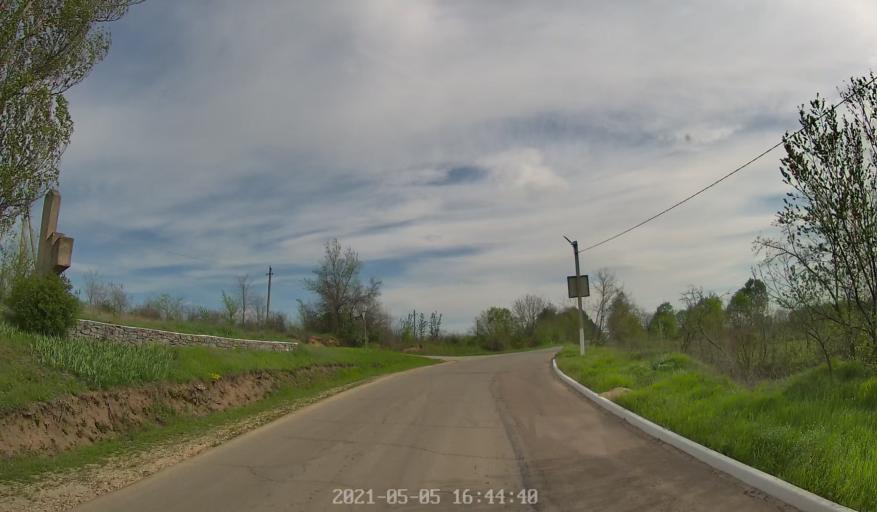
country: MD
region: Criuleni
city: Criuleni
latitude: 47.1159
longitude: 29.1945
